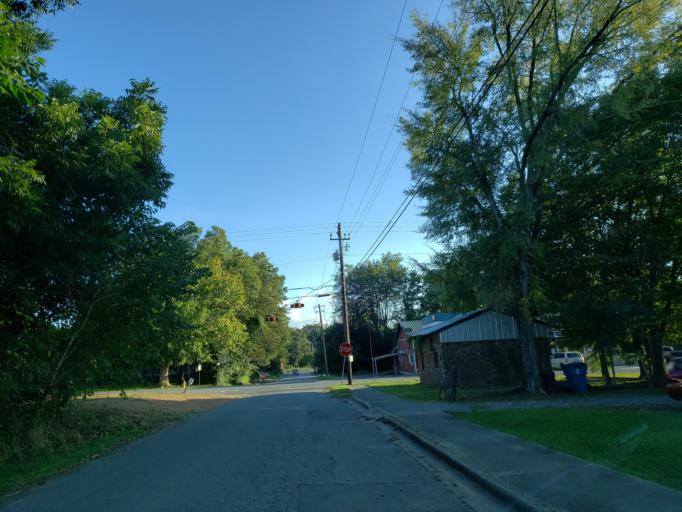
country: US
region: Georgia
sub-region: Bartow County
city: Euharlee
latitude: 34.2388
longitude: -84.9452
